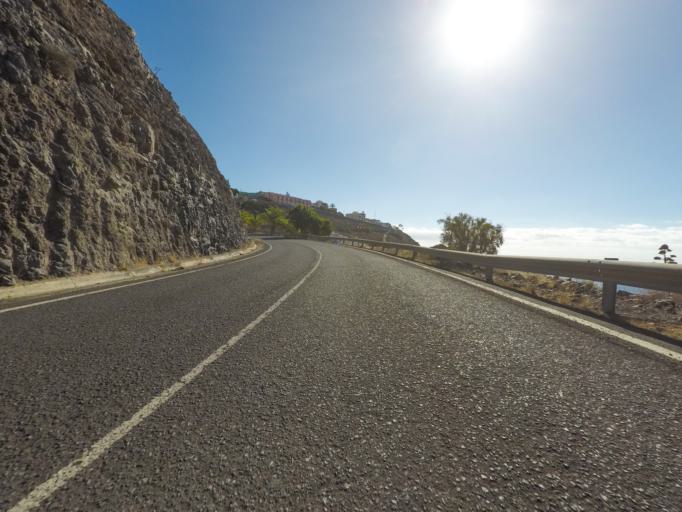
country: ES
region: Canary Islands
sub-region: Provincia de Santa Cruz de Tenerife
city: Alajero
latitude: 28.0335
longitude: -17.1946
